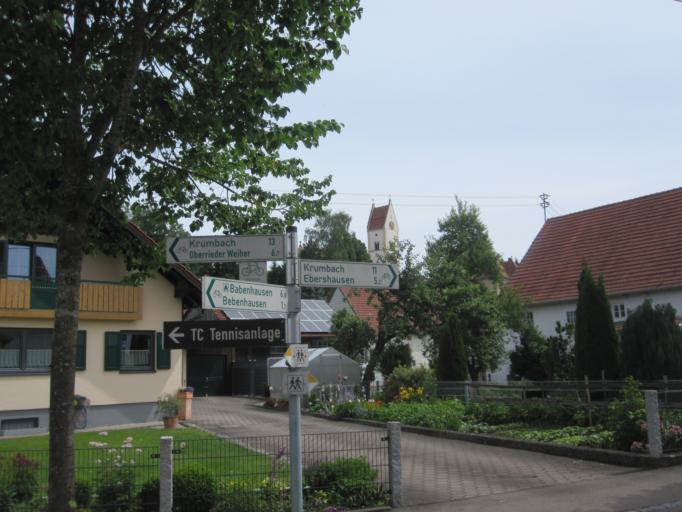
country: DE
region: Bavaria
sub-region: Swabia
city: Kettershausen
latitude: 48.1836
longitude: 10.2593
